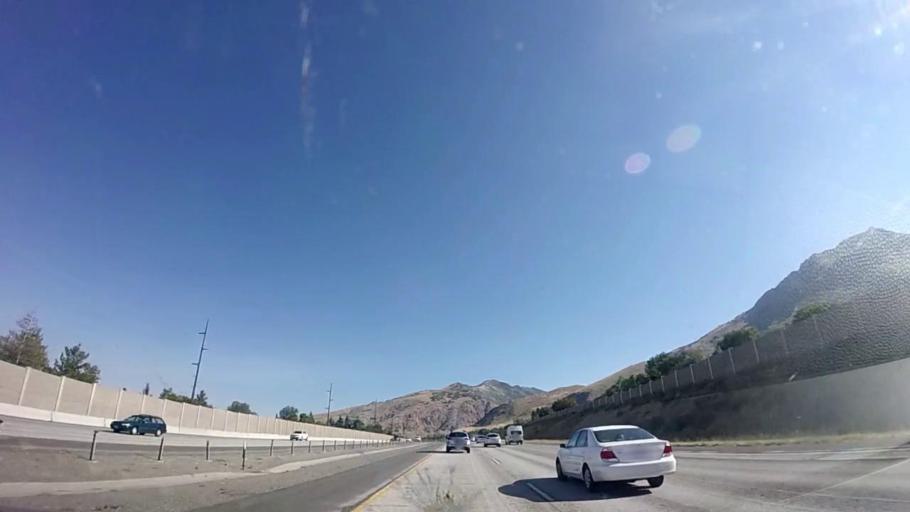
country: US
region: Utah
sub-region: Salt Lake County
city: Mount Olympus
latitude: 40.6945
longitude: -111.7962
